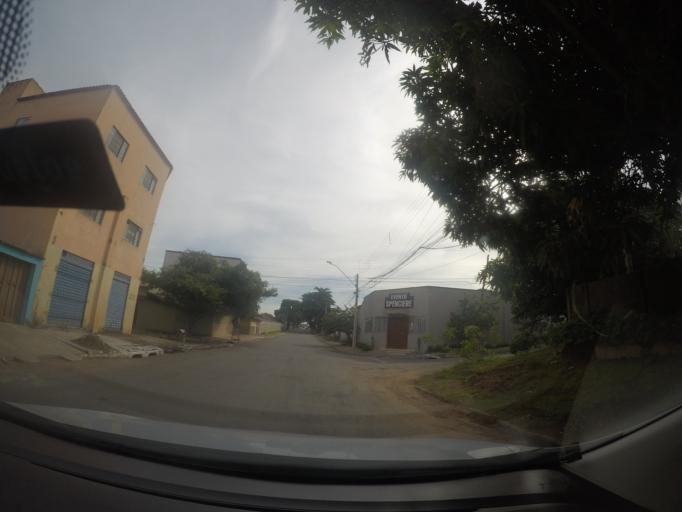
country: BR
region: Goias
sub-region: Goiania
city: Goiania
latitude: -16.6588
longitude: -49.3067
